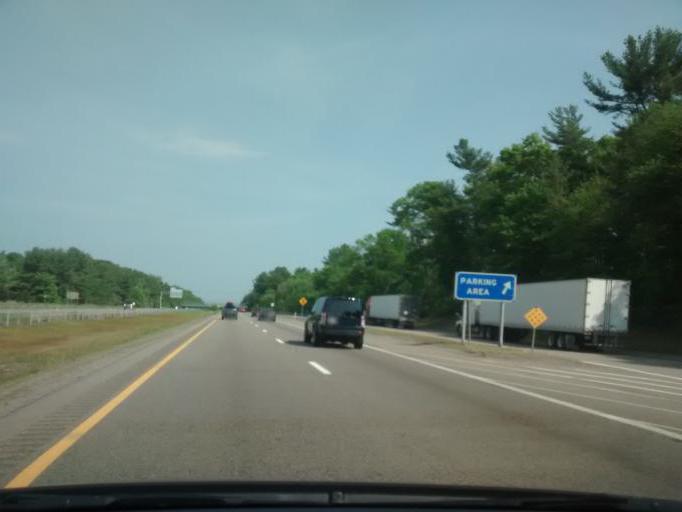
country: US
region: Massachusetts
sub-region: Plymouth County
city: Middleborough Center
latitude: 41.8775
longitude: -70.9092
